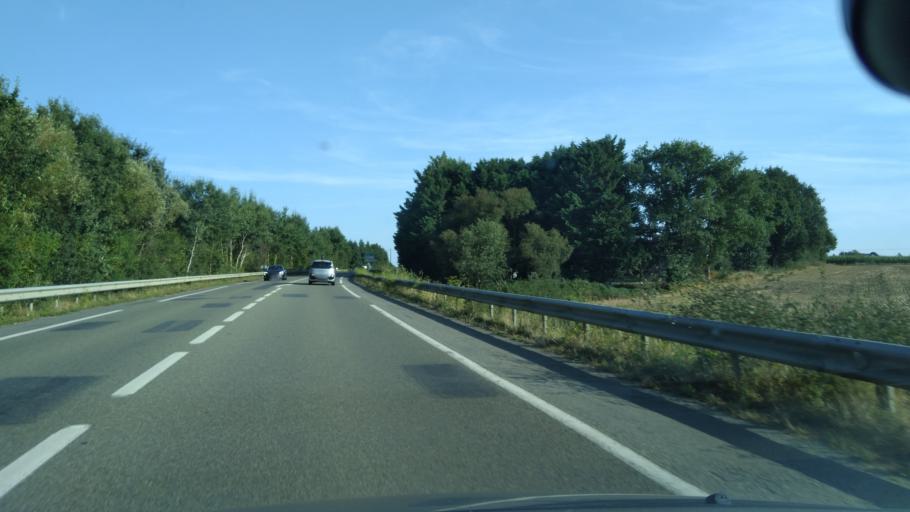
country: FR
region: Pays de la Loire
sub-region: Departement de la Mayenne
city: Entrammes
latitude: 47.9909
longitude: -0.7153
